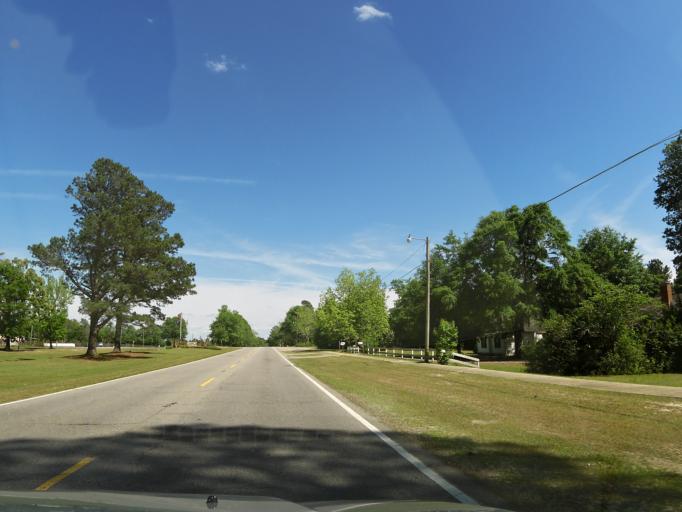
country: US
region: South Carolina
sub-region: Barnwell County
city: Williston
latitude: 33.3940
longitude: -81.4071
